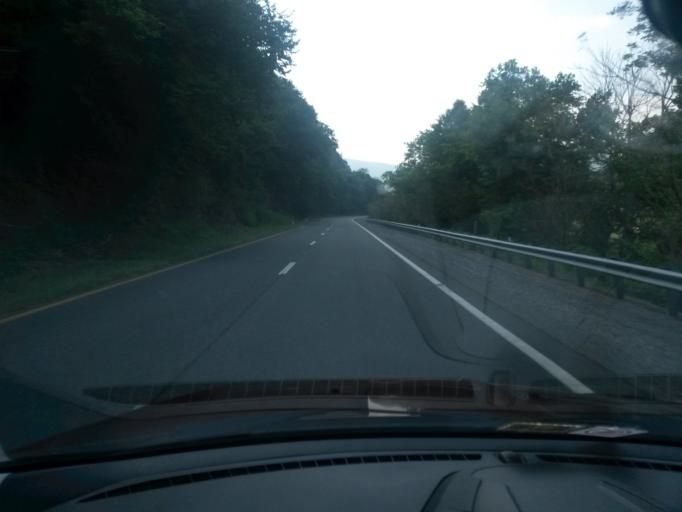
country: US
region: Virginia
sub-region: Giles County
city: Narrows
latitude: 37.3536
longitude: -80.8105
